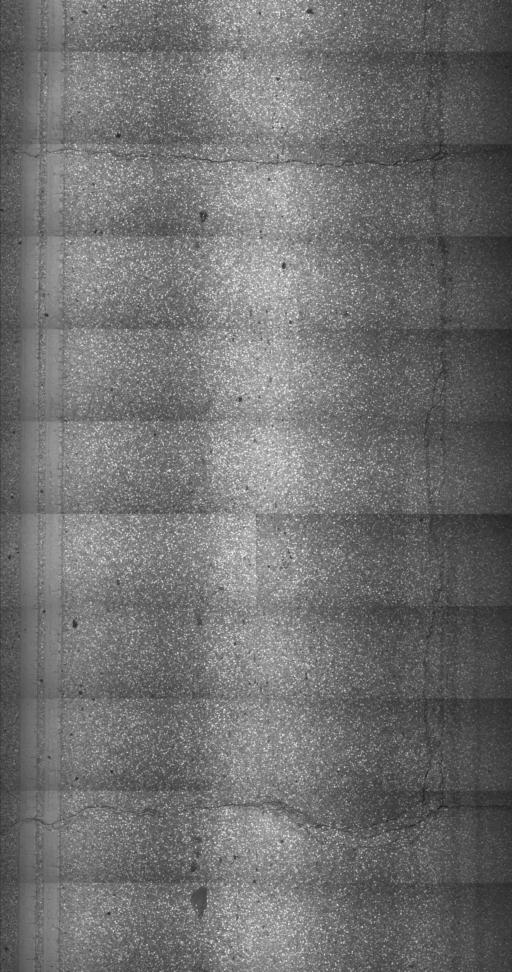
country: US
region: Vermont
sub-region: Franklin County
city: Swanton
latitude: 44.9162
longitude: -73.1208
